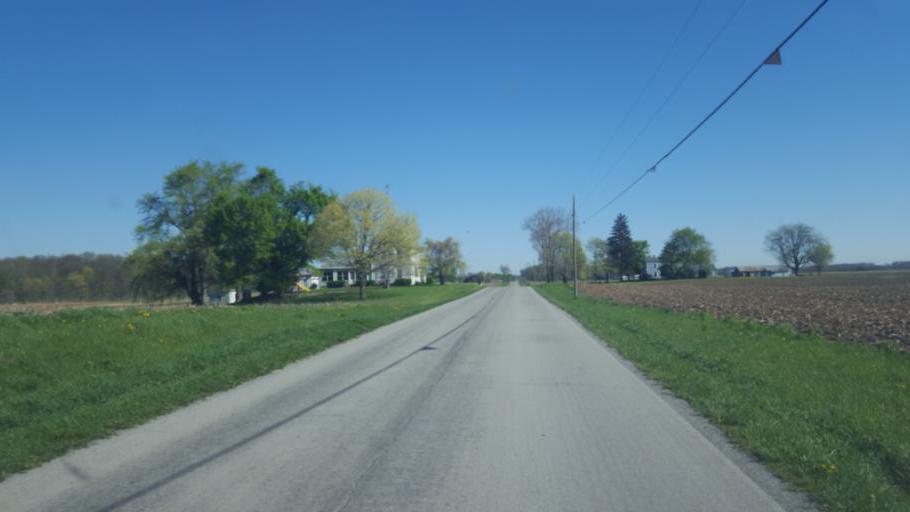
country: US
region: Ohio
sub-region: Wyandot County
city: Upper Sandusky
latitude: 40.8566
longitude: -83.2225
